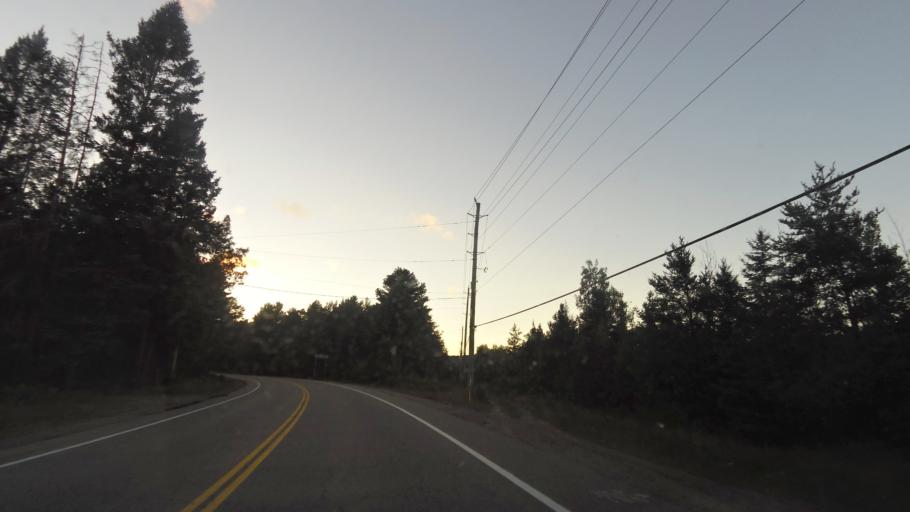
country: CA
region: Ontario
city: Bancroft
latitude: 45.0401
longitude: -78.4183
